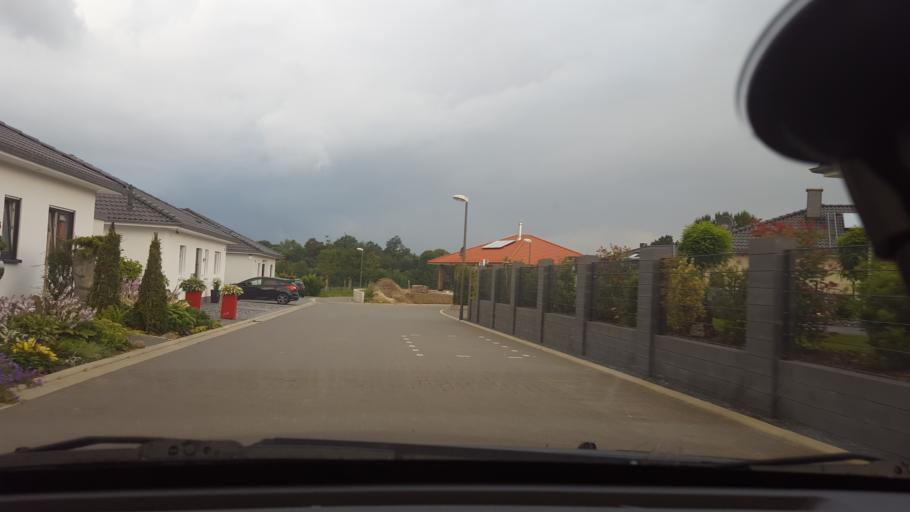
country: DE
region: North Rhine-Westphalia
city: Marl
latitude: 51.6537
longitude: 7.1414
